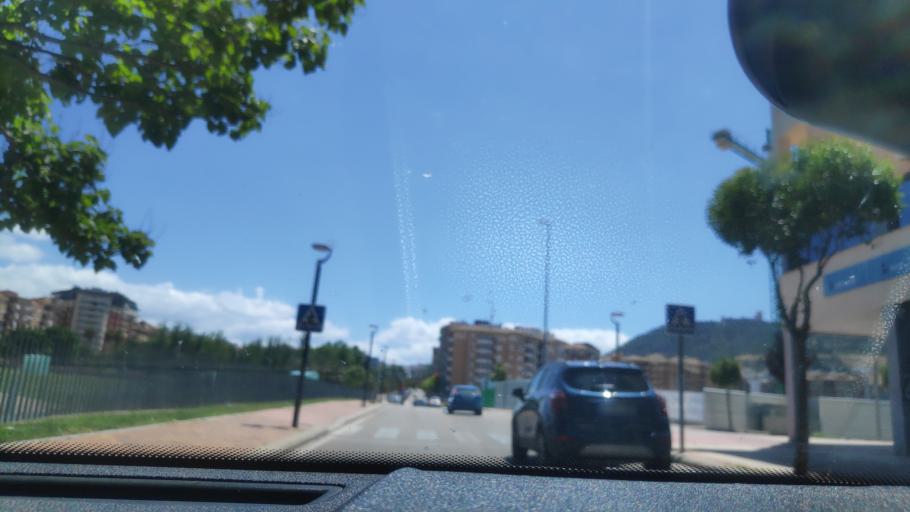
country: ES
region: Andalusia
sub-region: Provincia de Jaen
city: Jaen
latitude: 37.7853
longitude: -3.7914
